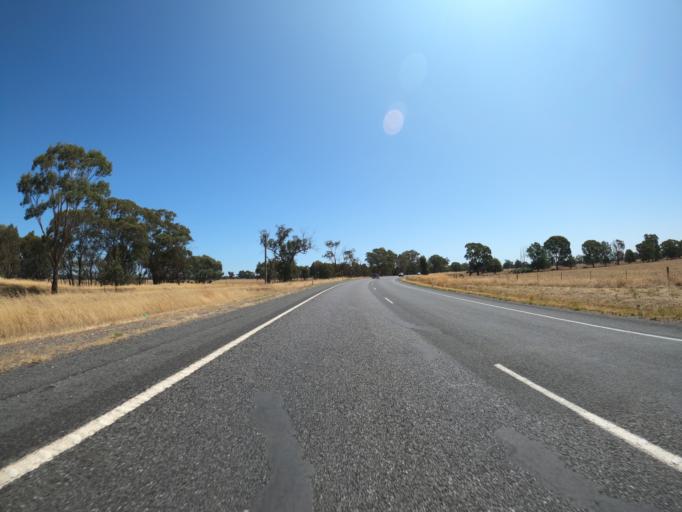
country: AU
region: New South Wales
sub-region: Corowa Shire
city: Corowa
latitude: -36.0669
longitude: 146.3920
